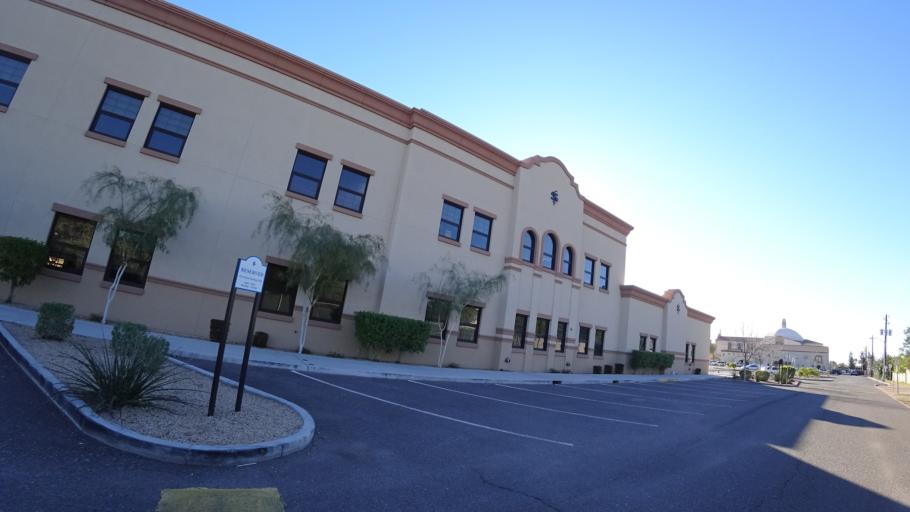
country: US
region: Arizona
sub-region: Maricopa County
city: Phoenix
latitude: 33.5064
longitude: -112.0706
